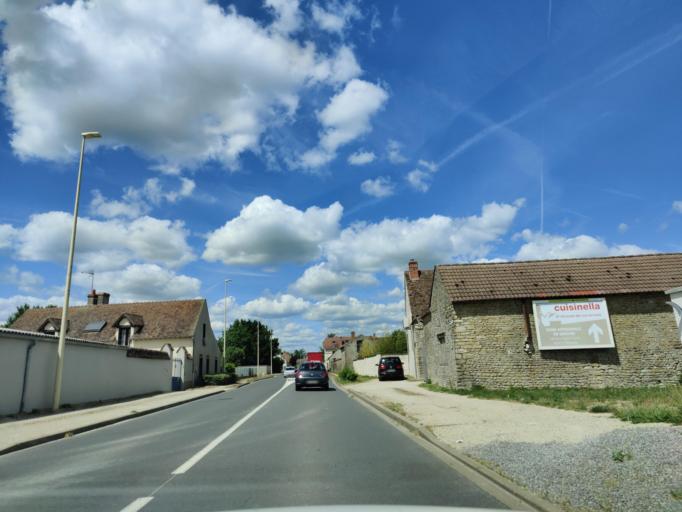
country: FR
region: Centre
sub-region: Departement du Loiret
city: Dadonville
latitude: 48.1216
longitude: 2.2512
